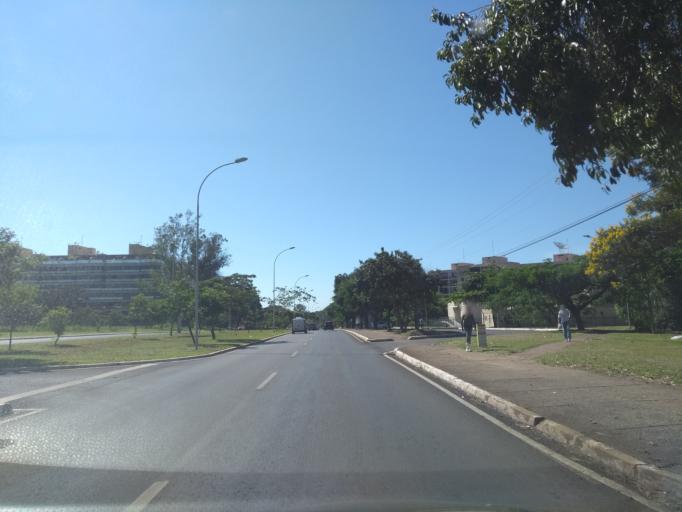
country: BR
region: Federal District
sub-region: Brasilia
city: Brasilia
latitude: -15.8053
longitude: -47.9385
